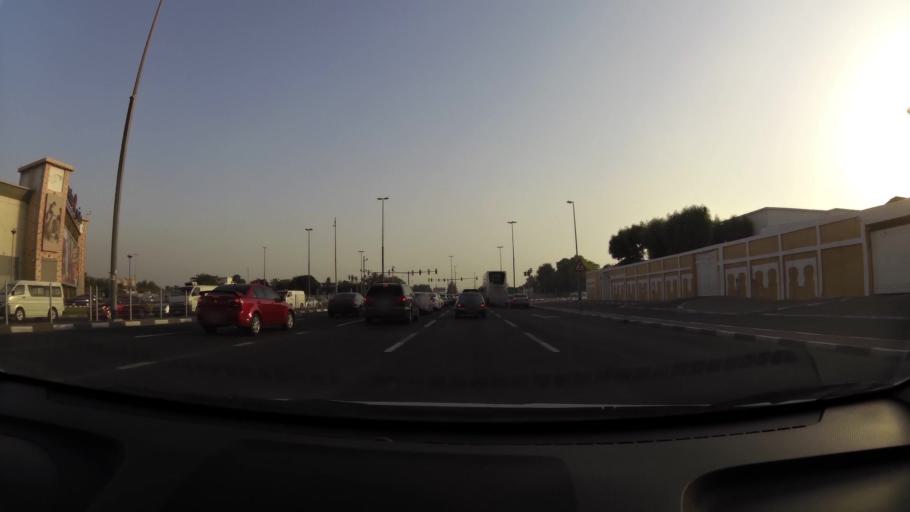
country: AE
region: Ash Shariqah
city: Sharjah
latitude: 25.2911
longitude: 55.3463
